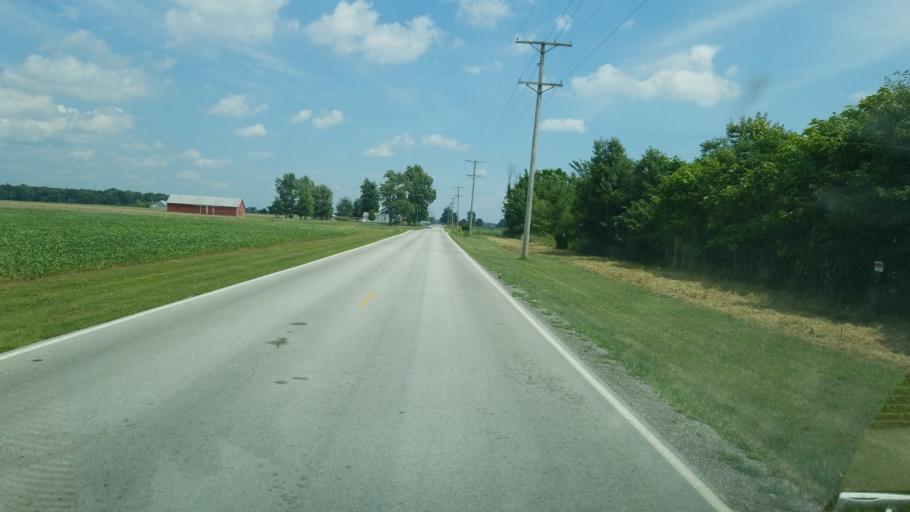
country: US
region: Ohio
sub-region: Hancock County
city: Arlington
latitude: 40.9065
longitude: -83.6071
